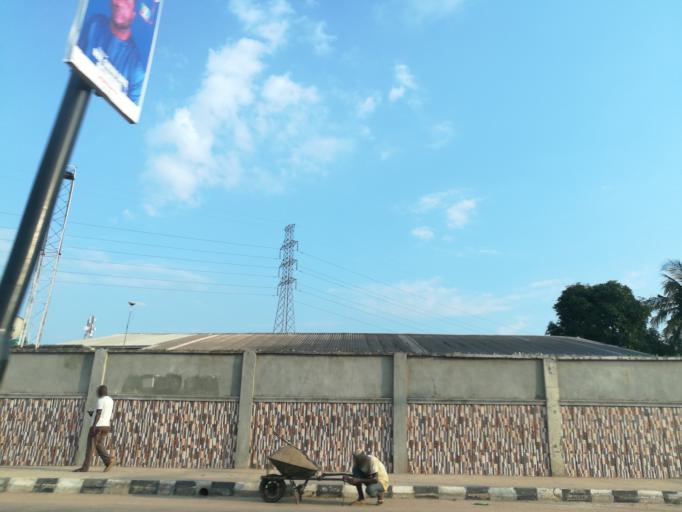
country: NG
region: Lagos
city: Ojota
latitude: 6.5874
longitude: 3.3954
